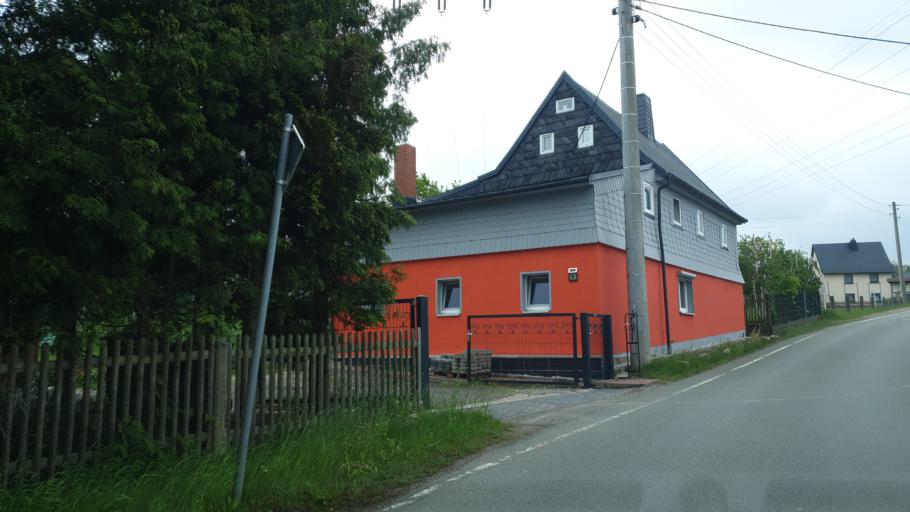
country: DE
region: Saxony
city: Hartmannsdorf
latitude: 50.8610
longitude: 12.8090
